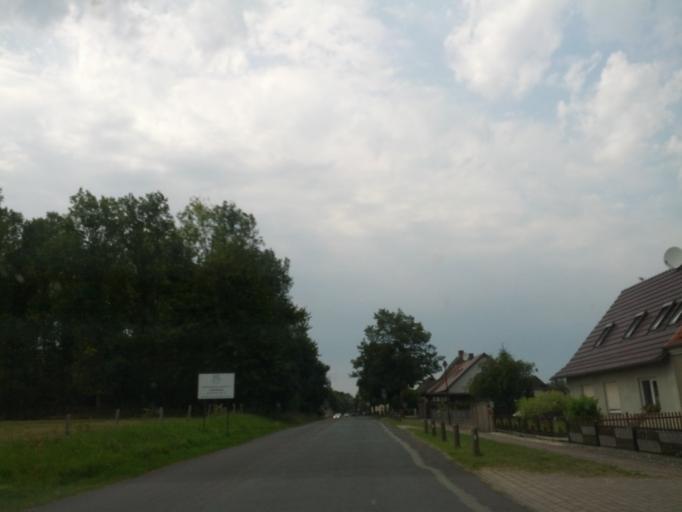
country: DE
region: Brandenburg
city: Kremmen
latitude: 52.7552
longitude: 12.8911
